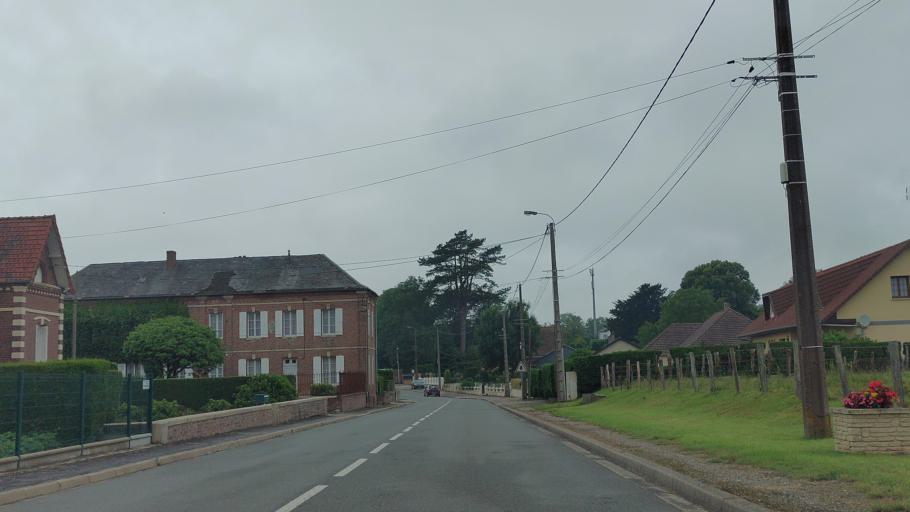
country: FR
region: Picardie
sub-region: Departement de la Somme
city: Bethencourt-sur-Mer
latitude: 50.0877
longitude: 1.4848
